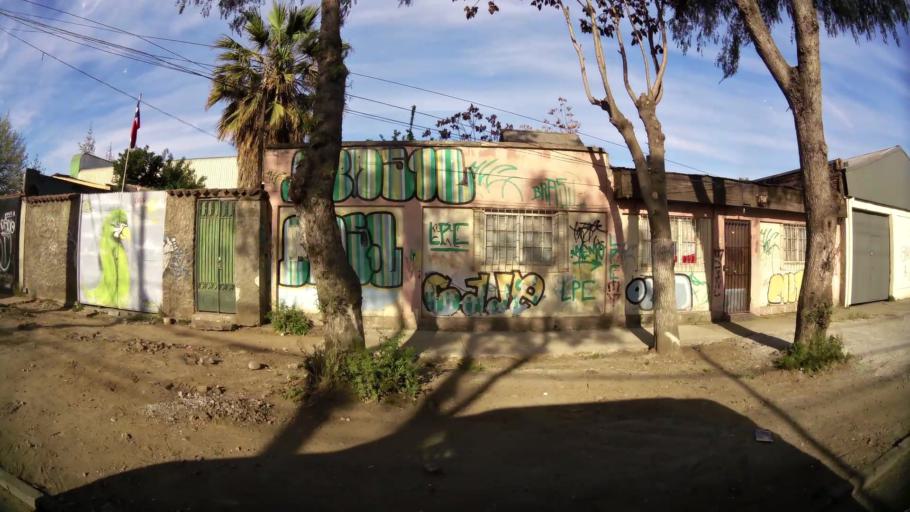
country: CL
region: Santiago Metropolitan
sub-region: Provincia de Santiago
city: Lo Prado
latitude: -33.4365
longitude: -70.7071
